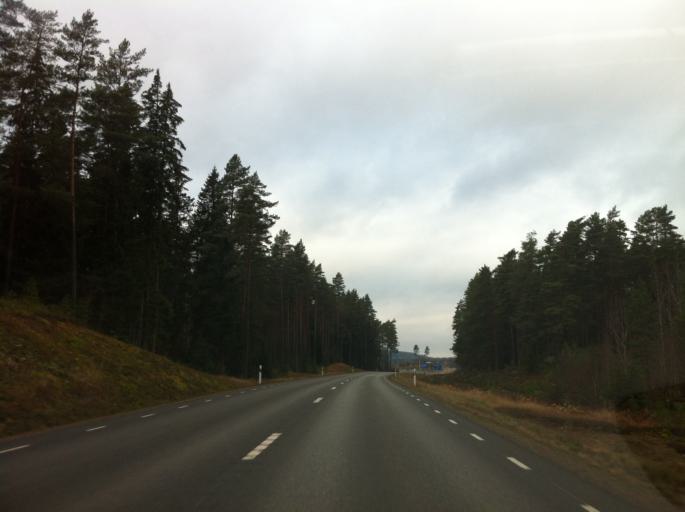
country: SE
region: Joenkoeping
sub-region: Vetlanda Kommun
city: Vetlanda
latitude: 57.4113
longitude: 15.2734
